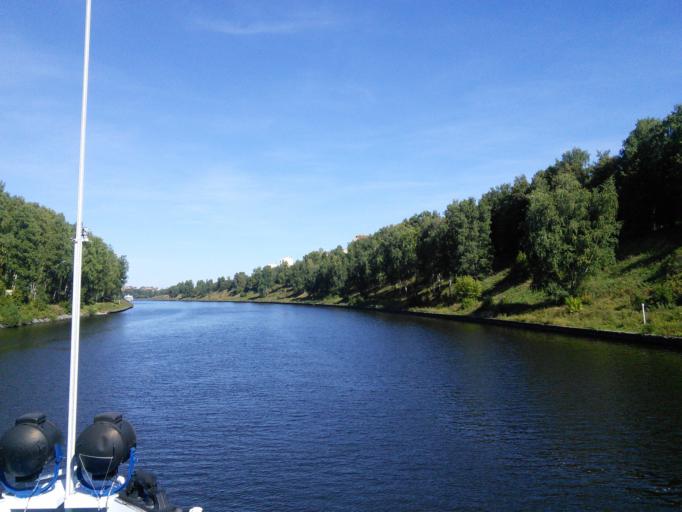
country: RU
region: Moskovskaya
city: Dolgoprudnyy
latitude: 55.9310
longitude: 37.4887
